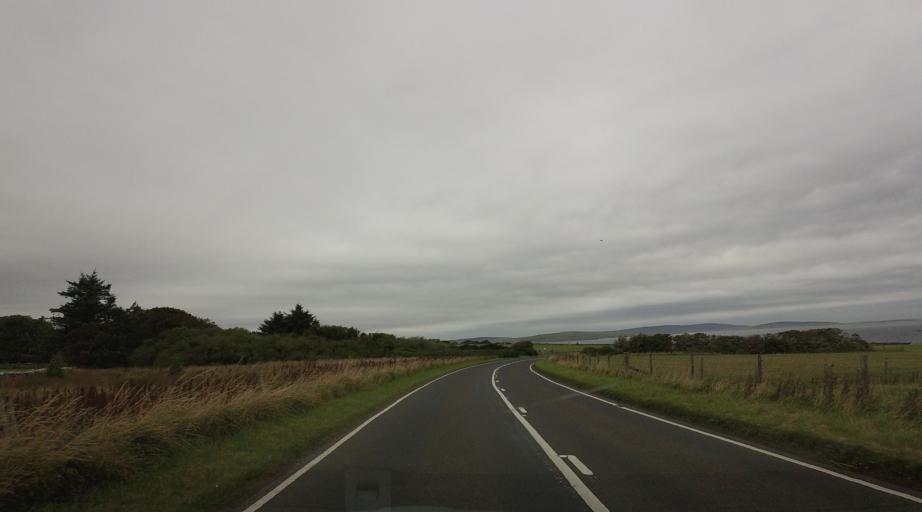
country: GB
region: Scotland
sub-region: Orkney Islands
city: Orkney
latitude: 58.9929
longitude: -2.9936
